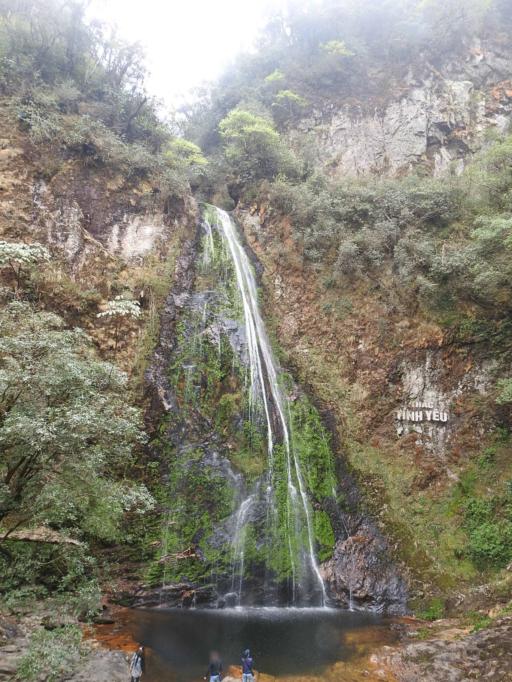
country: VN
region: Lao Cai
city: Sa Pa
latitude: 22.3475
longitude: 103.7722
